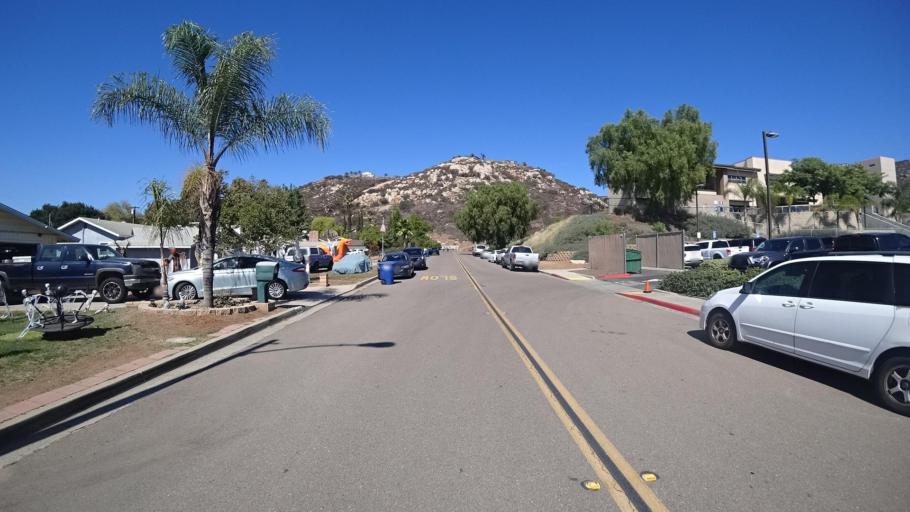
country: US
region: California
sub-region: San Diego County
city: Winter Gardens
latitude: 32.8278
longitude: -116.9541
